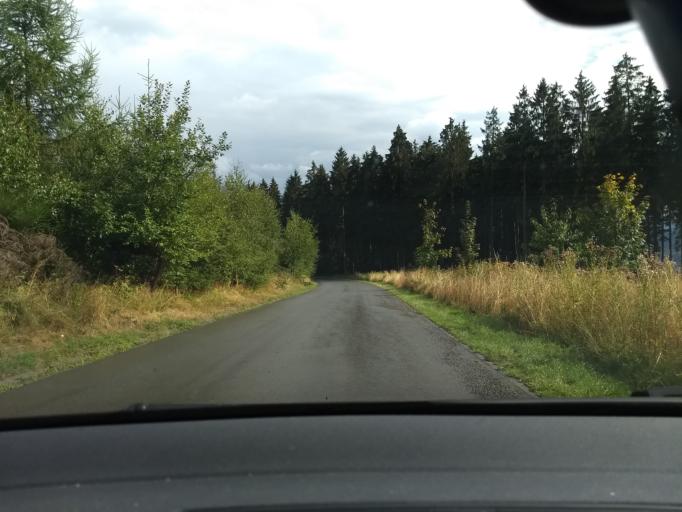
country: DE
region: North Rhine-Westphalia
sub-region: Regierungsbezirk Arnsberg
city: Finnentrop
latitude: 51.2129
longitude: 7.9998
